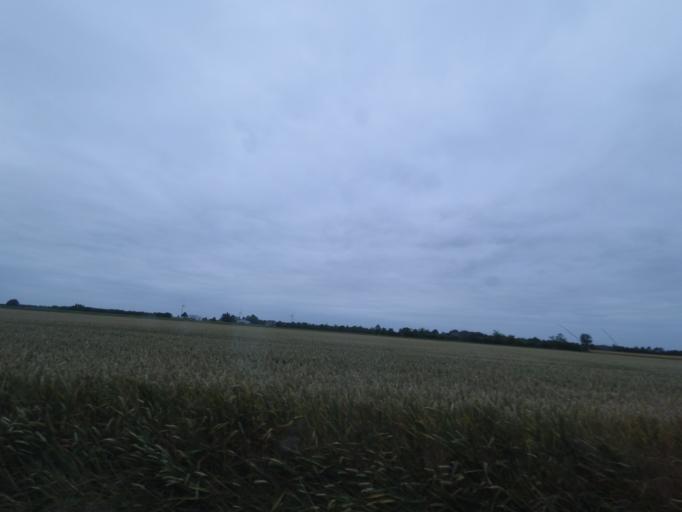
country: DK
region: South Denmark
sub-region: Nordfyns Kommune
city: Otterup
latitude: 55.5590
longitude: 10.4301
